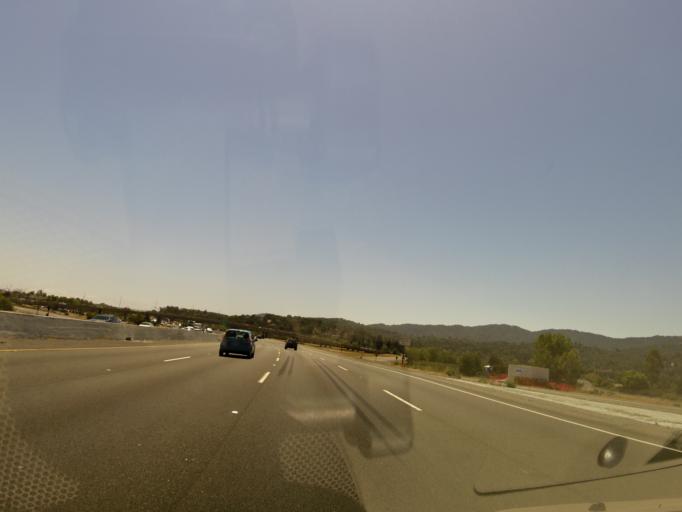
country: US
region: California
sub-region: Marin County
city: Novato
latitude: 38.0952
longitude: -122.5614
